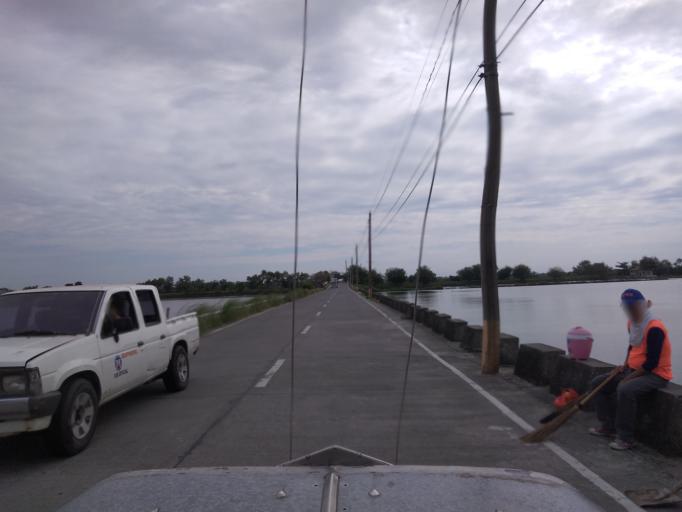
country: PH
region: Central Luzon
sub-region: Province of Pampanga
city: Lubao
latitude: 14.9380
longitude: 120.6106
